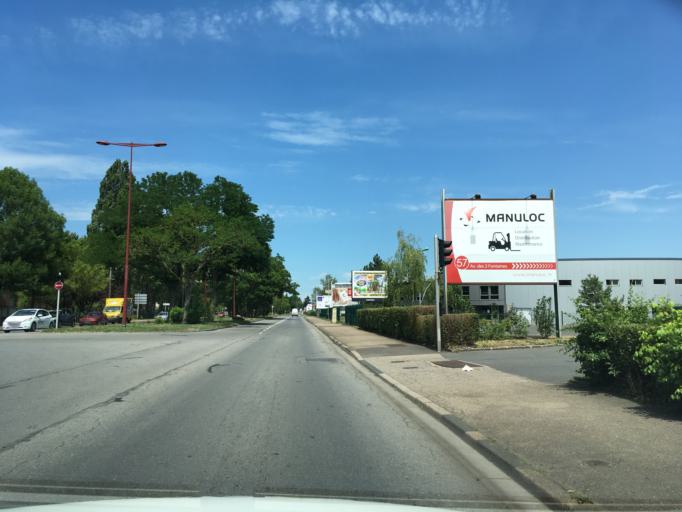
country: FR
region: Lorraine
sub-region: Departement de la Moselle
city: Metz
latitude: 49.1431
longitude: 6.1723
